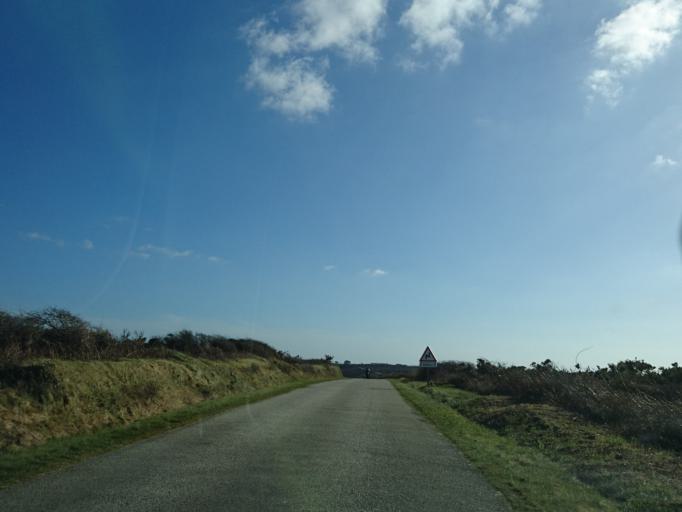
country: FR
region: Brittany
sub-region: Departement du Finistere
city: Roscanvel
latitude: 48.3132
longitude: -4.5711
